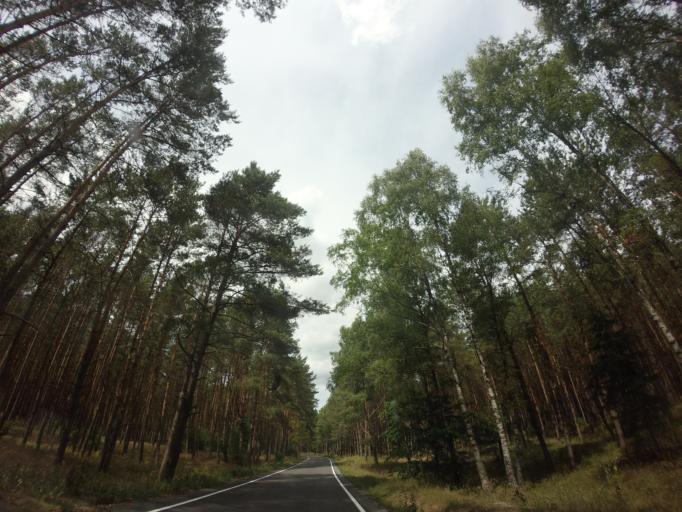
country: PL
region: West Pomeranian Voivodeship
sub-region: Powiat choszczenski
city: Drawno
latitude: 53.1283
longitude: 15.7267
